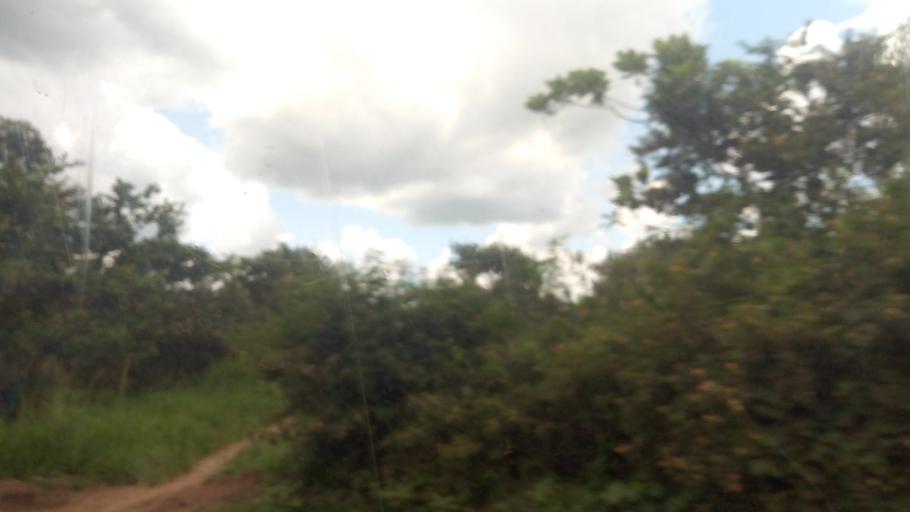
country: UG
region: Western Region
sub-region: Kiryandongo District
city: Kiryandongo
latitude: 1.9285
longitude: 32.1326
